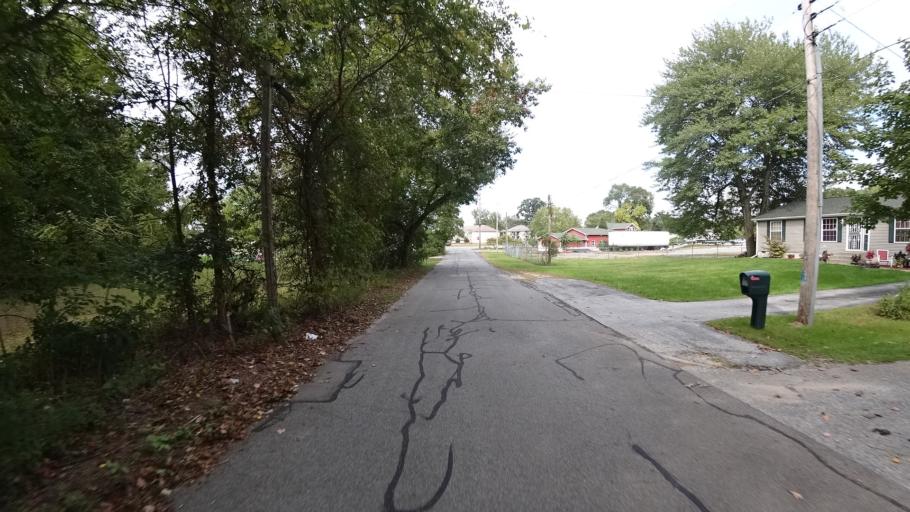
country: US
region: Indiana
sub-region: LaPorte County
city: Long Beach
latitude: 41.7348
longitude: -86.8507
